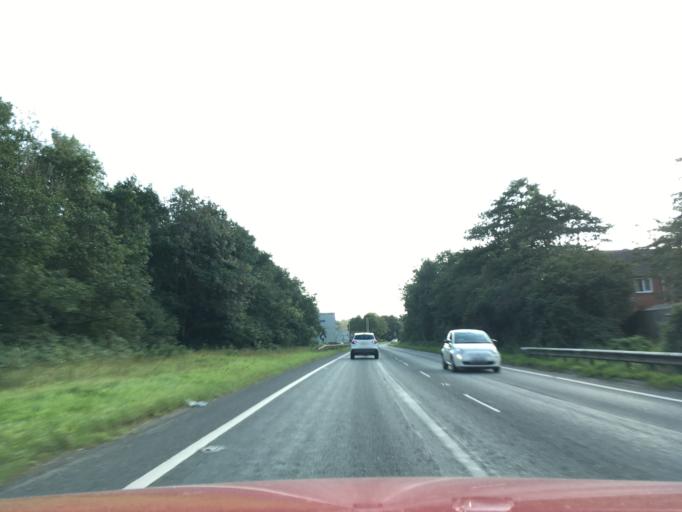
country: GB
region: Wales
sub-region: Rhondda Cynon Taf
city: Llantrisant
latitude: 51.5382
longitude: -3.3610
